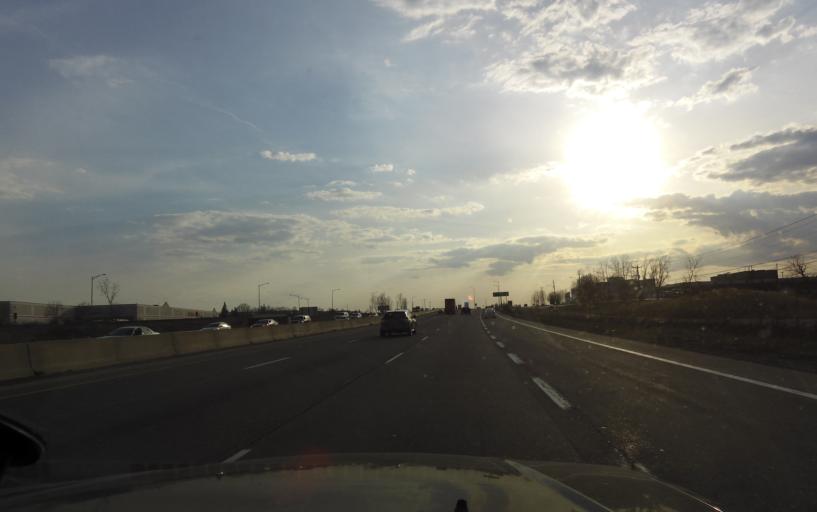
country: CA
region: Ontario
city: Oshawa
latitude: 43.8713
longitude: -78.8969
